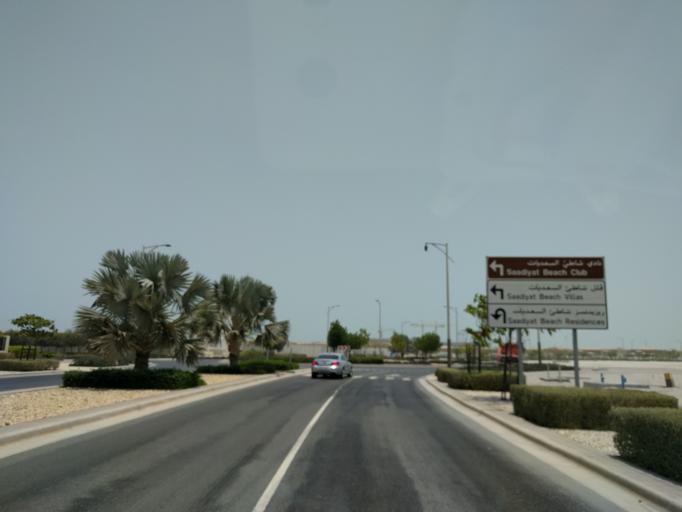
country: AE
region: Abu Dhabi
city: Abu Dhabi
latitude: 24.5526
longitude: 54.4527
